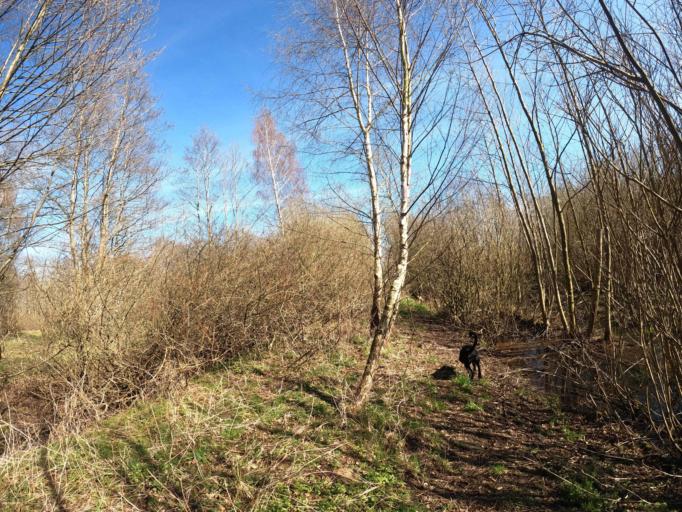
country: PL
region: West Pomeranian Voivodeship
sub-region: Powiat gryficki
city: Brojce
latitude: 53.9256
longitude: 15.2962
